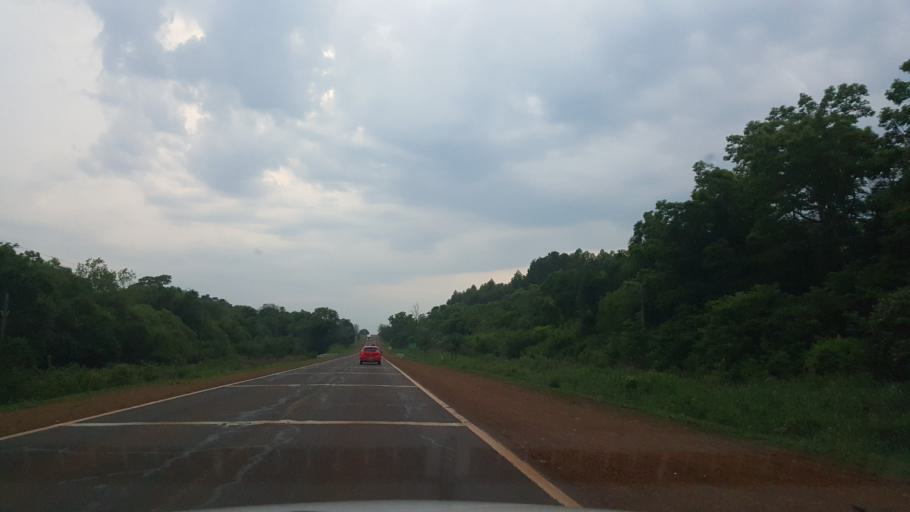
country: AR
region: Misiones
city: Santo Pipo
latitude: -27.1407
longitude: -55.4030
